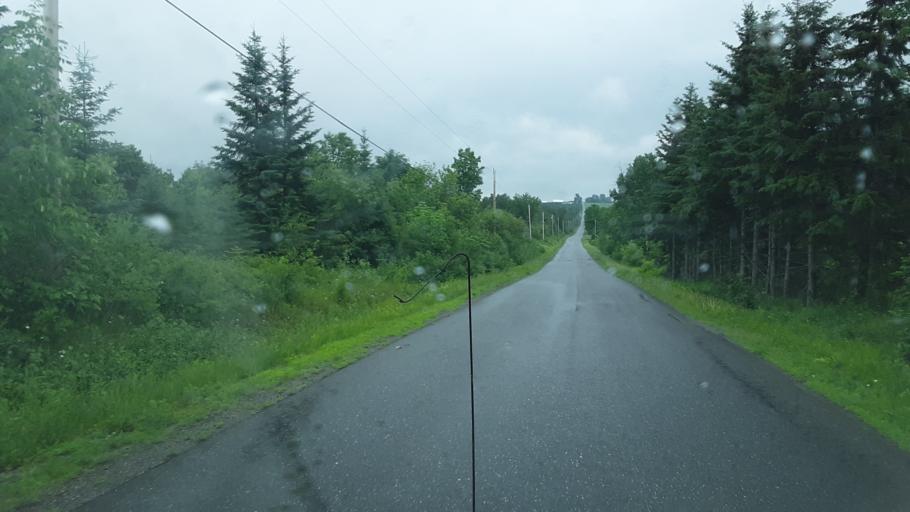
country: US
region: Maine
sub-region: Aroostook County
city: Presque Isle
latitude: 46.6813
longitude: -68.2143
